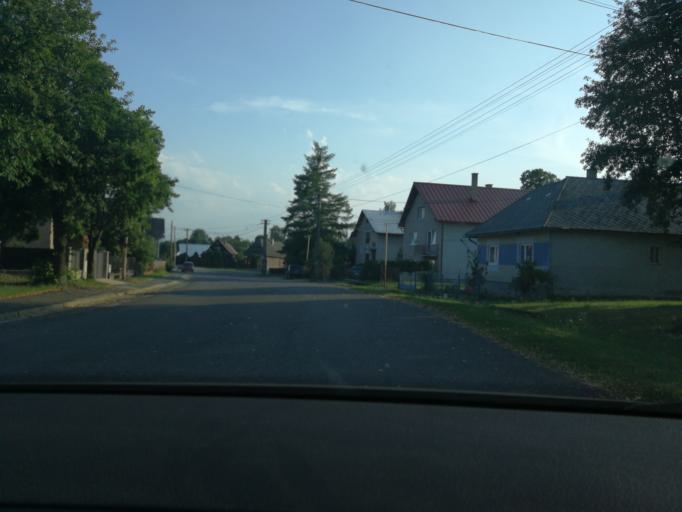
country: SK
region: Zilinsky
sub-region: Okres Liptovsky Mikulas
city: Liptovsky Mikulas
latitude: 49.1657
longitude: 19.5421
